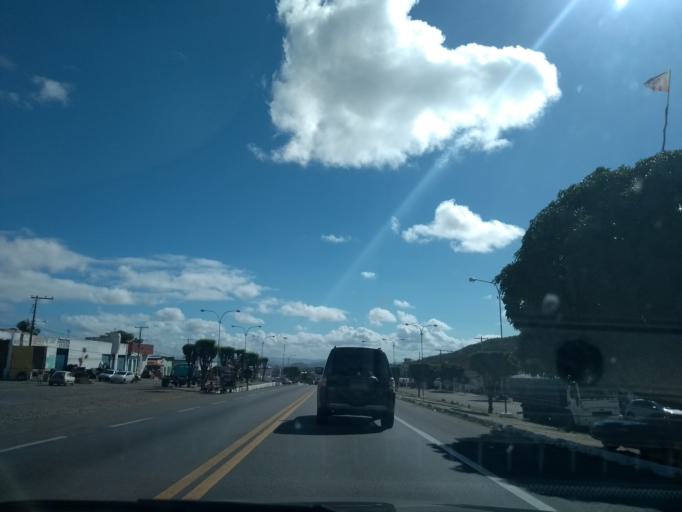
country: BR
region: Bahia
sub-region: Amargosa
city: Amargosa
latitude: -12.8755
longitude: -39.8571
